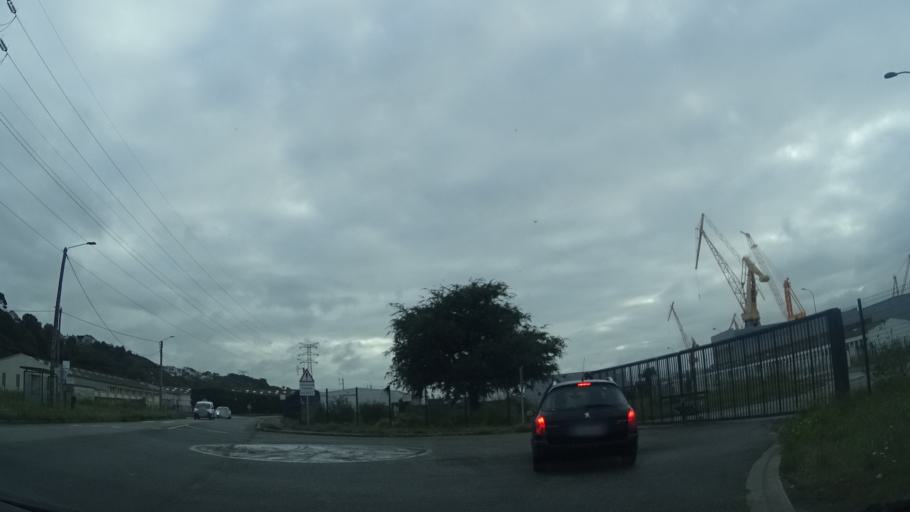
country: FR
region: Brittany
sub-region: Departement du Finistere
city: Brest
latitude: 48.3867
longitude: -4.4630
